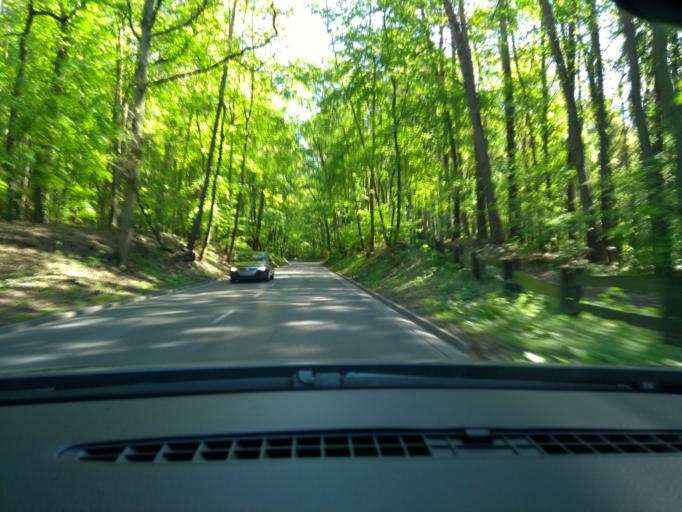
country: PL
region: West Pomeranian Voivodeship
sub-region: Szczecin
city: Szczecin
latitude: 53.4747
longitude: 14.4980
